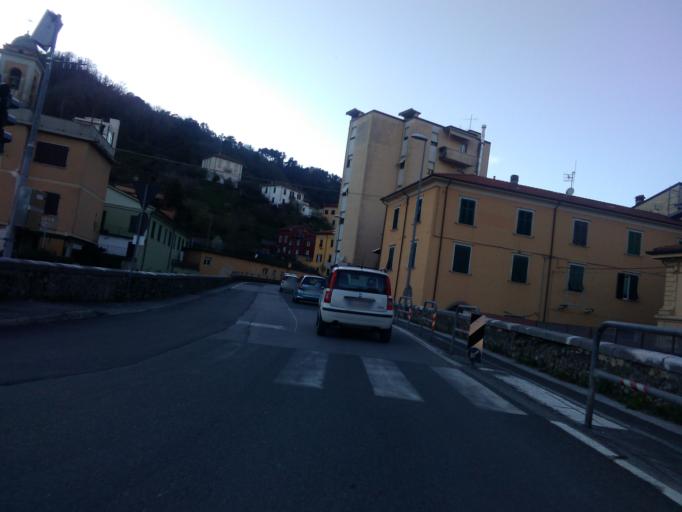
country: IT
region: Tuscany
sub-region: Provincia di Massa-Carrara
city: Carrara
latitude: 44.0801
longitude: 10.0959
